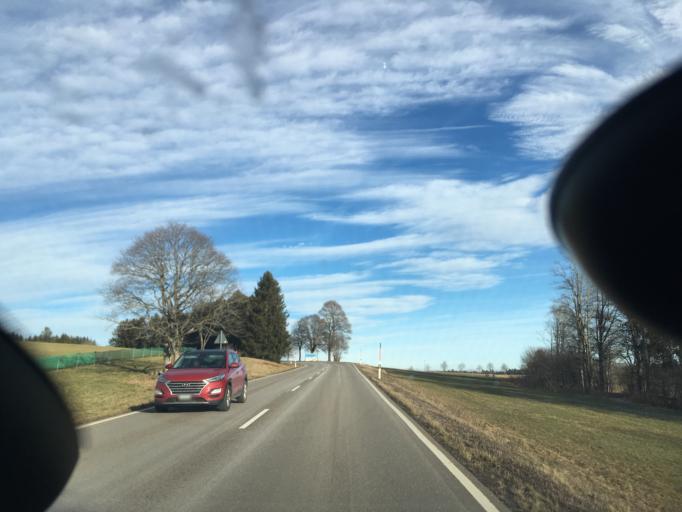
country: DE
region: Baden-Wuerttemberg
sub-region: Freiburg Region
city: Hochenschwand
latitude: 47.7271
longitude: 8.1596
